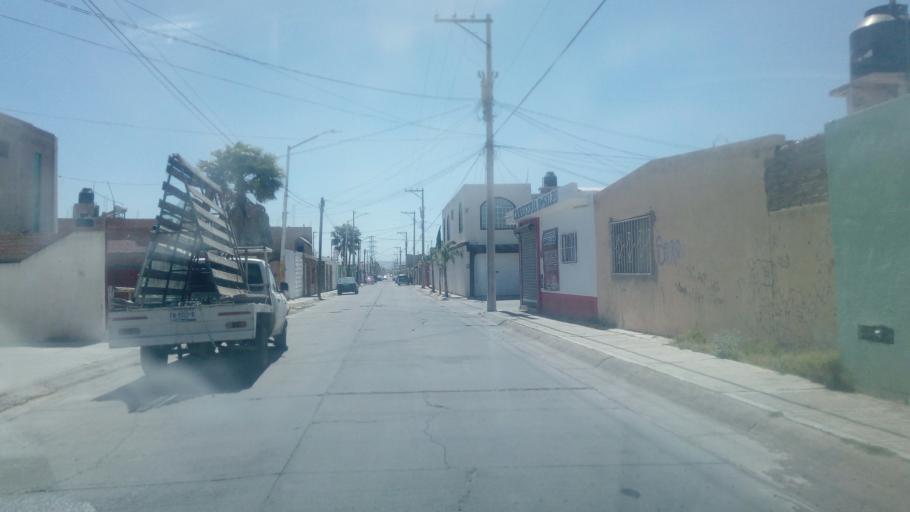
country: MX
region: Durango
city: Victoria de Durango
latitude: 24.0036
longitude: -104.6264
